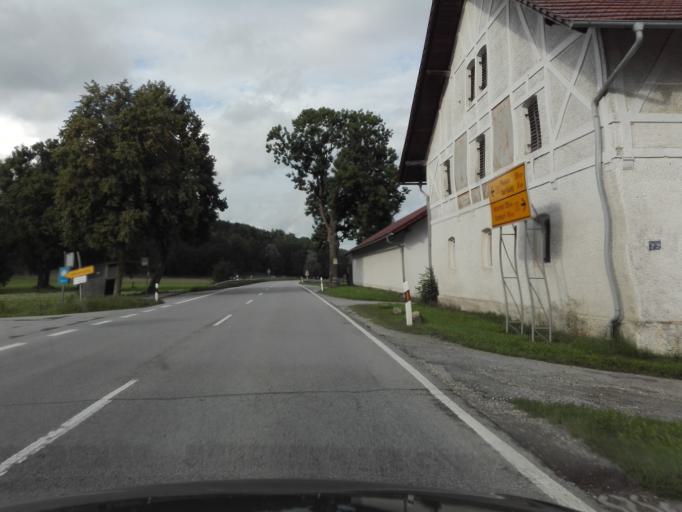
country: DE
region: Bavaria
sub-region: Lower Bavaria
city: Rotthalmunster
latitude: 48.3347
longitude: 13.2277
